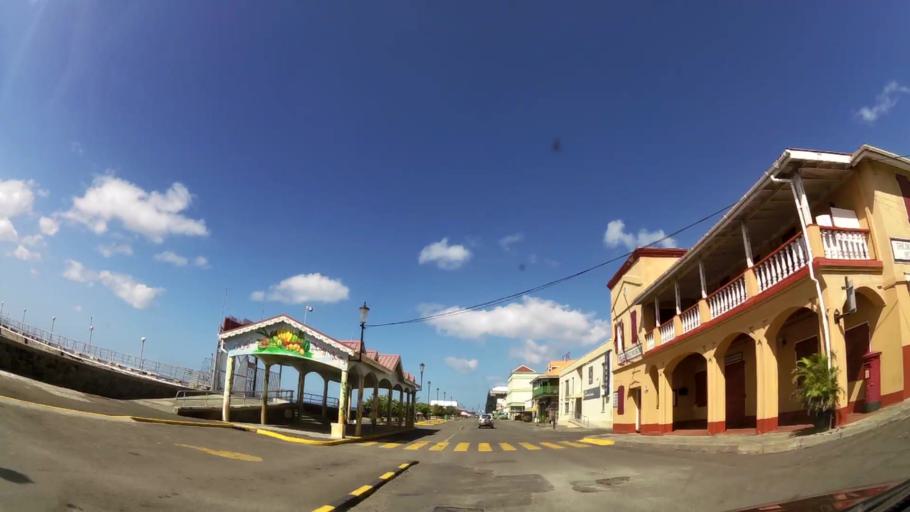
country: DM
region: Saint George
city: Roseau
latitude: 15.2964
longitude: -61.3876
